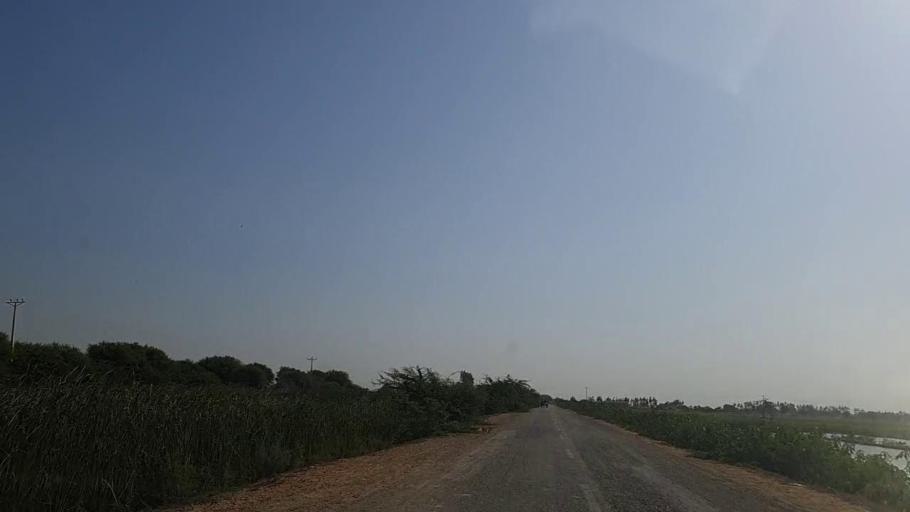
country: PK
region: Sindh
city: Jati
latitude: 24.4957
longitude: 68.2750
